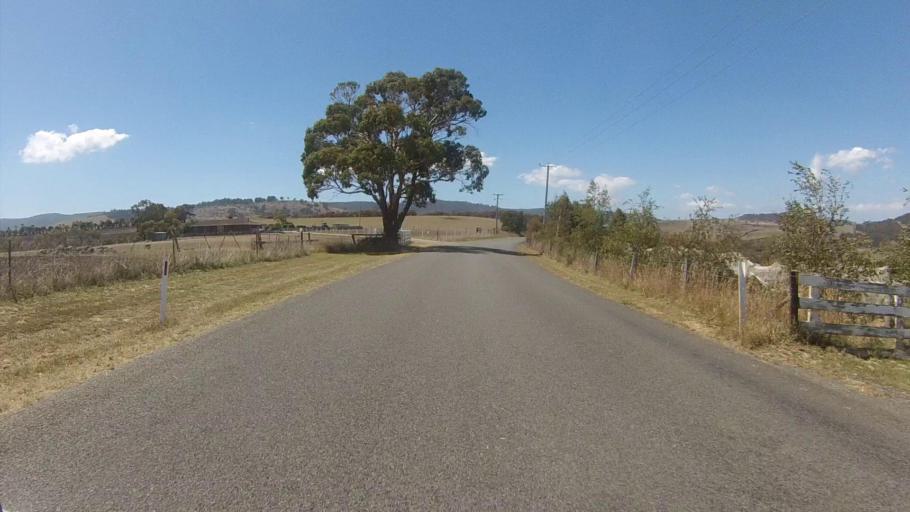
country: AU
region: Tasmania
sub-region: Sorell
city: Sorell
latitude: -42.7737
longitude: 147.5822
